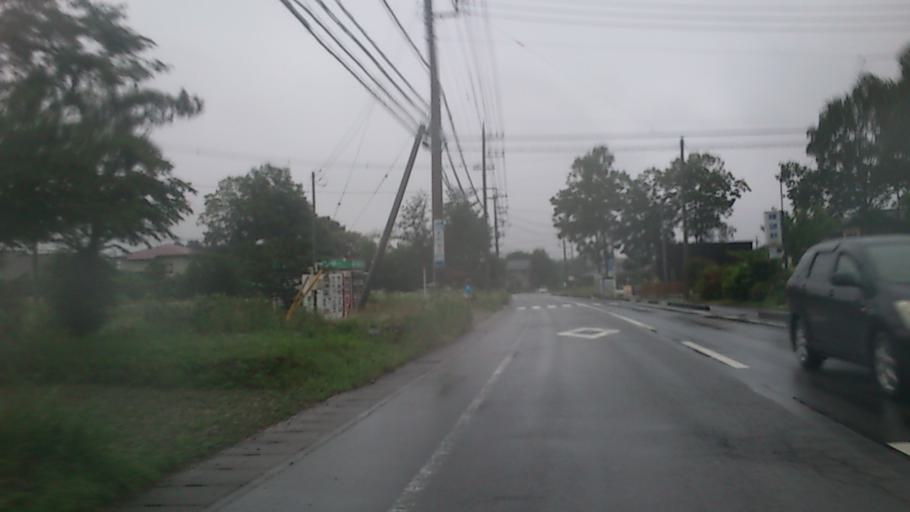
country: JP
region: Tochigi
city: Otawara
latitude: 36.9129
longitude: 139.9795
